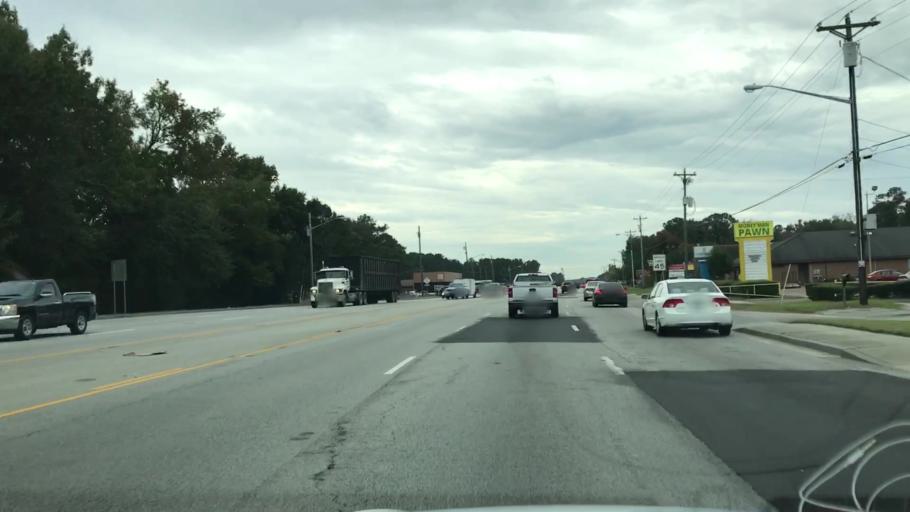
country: US
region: South Carolina
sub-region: Berkeley County
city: Goose Creek
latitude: 32.9929
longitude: -80.0393
